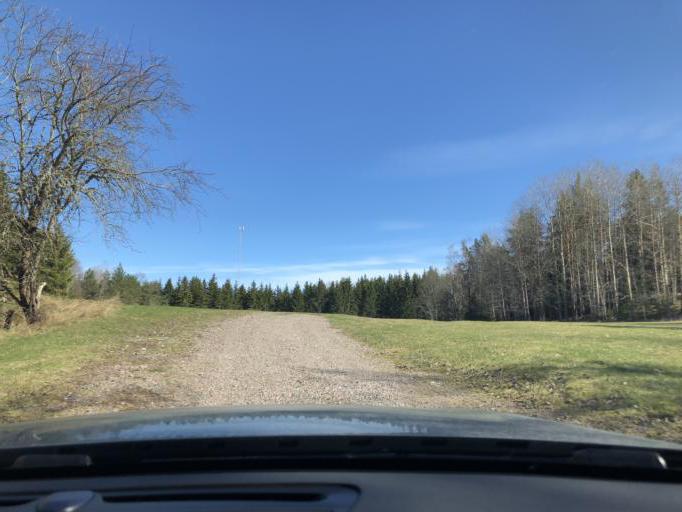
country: SE
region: Soedermanland
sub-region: Trosa Kommun
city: Vagnharad
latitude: 58.9345
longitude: 17.5250
